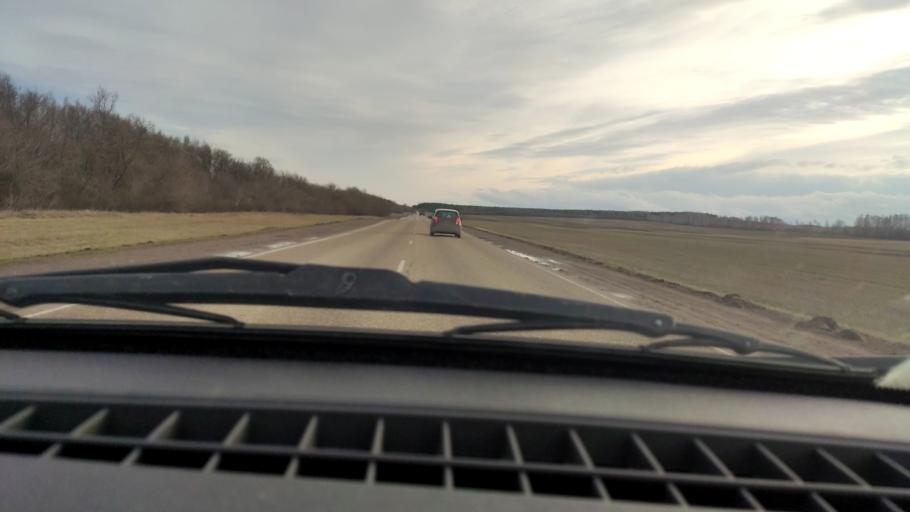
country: RU
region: Bashkortostan
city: Davlekanovo
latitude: 54.2569
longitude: 55.0864
